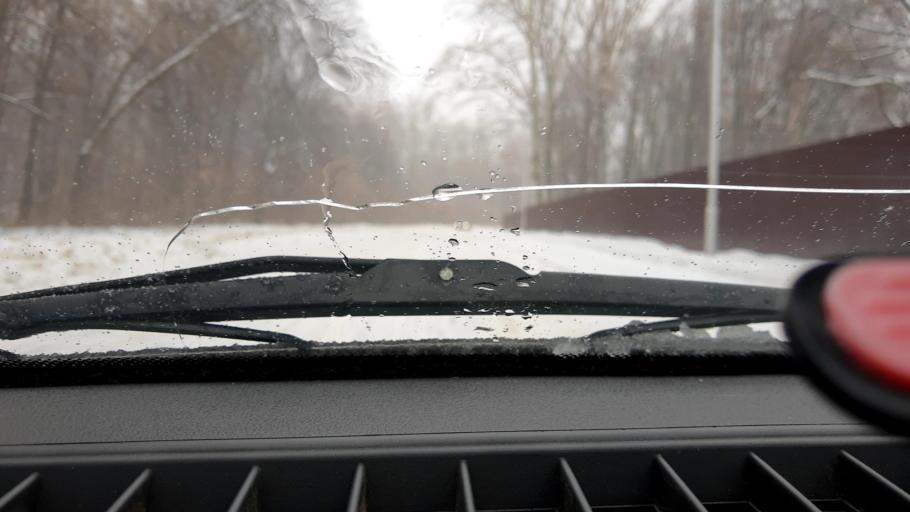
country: RU
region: Bashkortostan
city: Ufa
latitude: 54.8111
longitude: 56.0448
